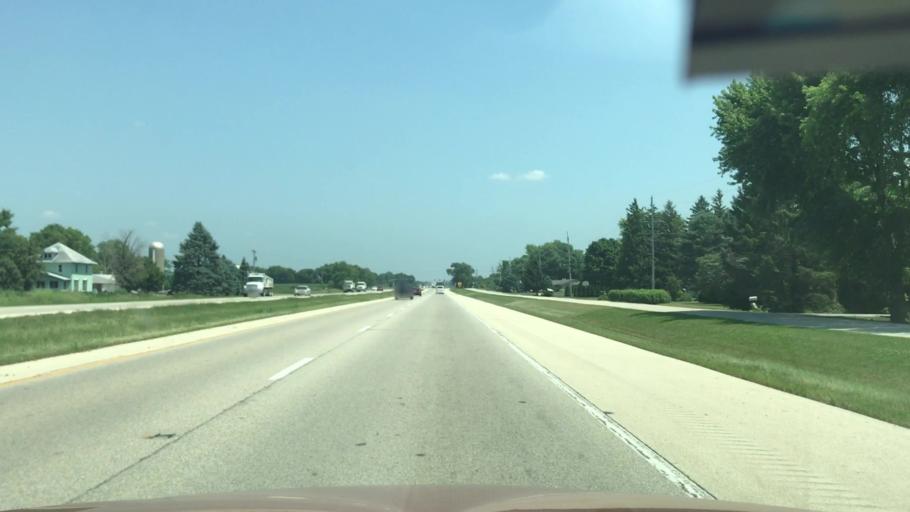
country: US
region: Illinois
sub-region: Winnebago County
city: Cherry Valley
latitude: 42.2398
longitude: -88.9086
